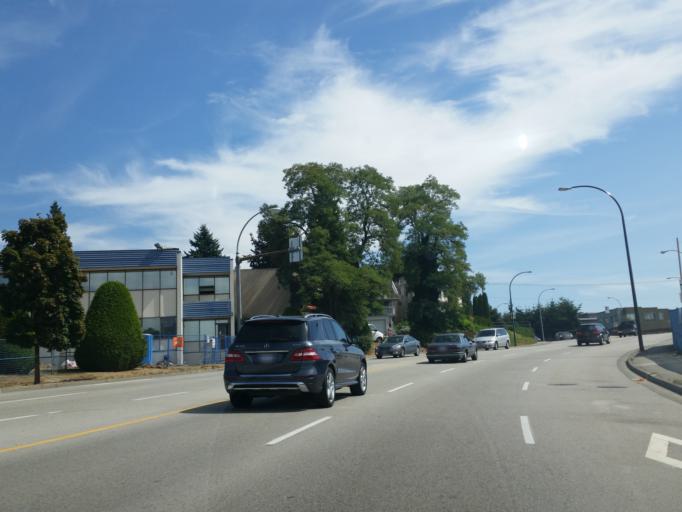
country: CA
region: British Columbia
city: Burnaby
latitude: 49.2808
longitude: -122.9938
